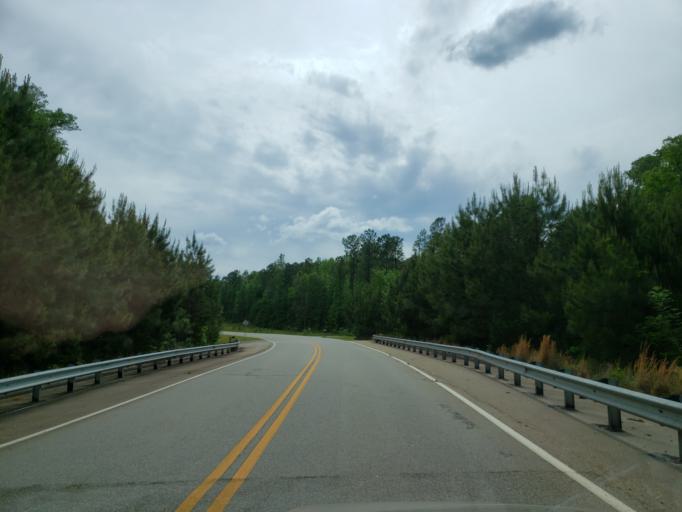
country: US
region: Georgia
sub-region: Monroe County
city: Forsyth
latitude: 32.9586
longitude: -83.9169
